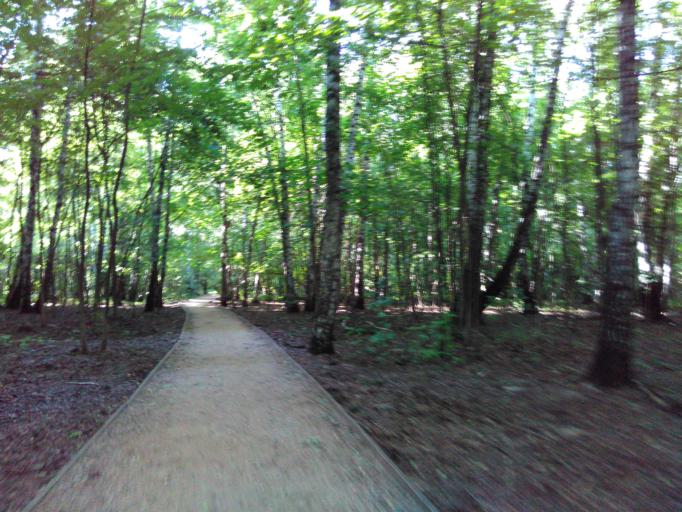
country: RU
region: Moscow
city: Troparevo
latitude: 55.6591
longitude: 37.4987
